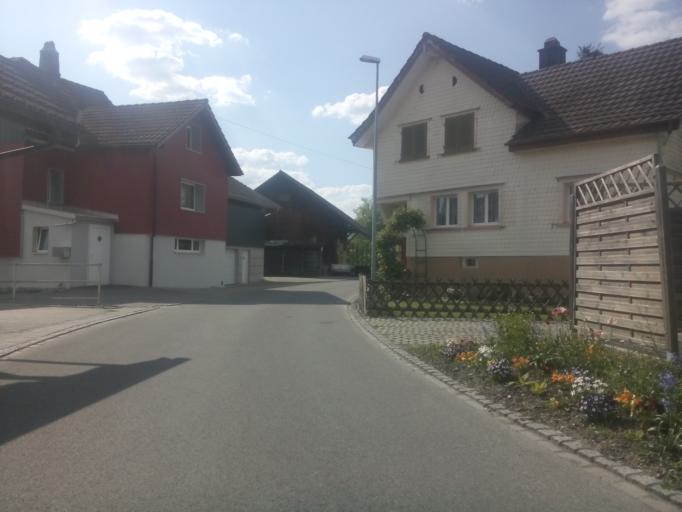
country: AT
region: Vorarlberg
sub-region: Politischer Bezirk Feldkirch
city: Koblach
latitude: 47.3306
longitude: 9.5864
